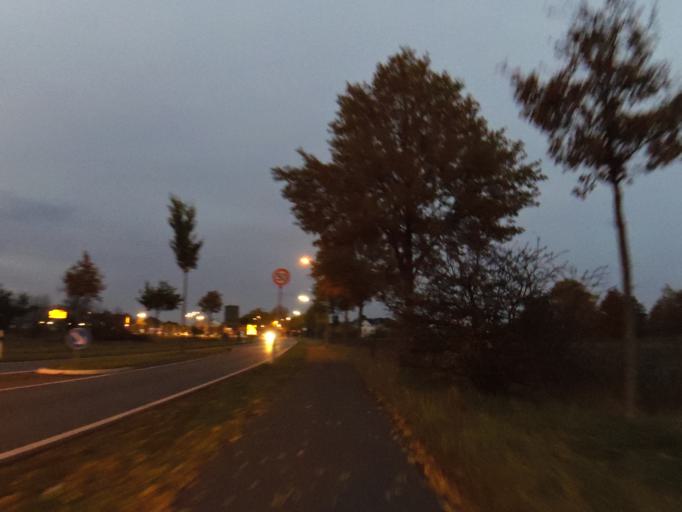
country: DE
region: Hesse
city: Morfelden-Walldorf
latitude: 49.9932
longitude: 8.5626
